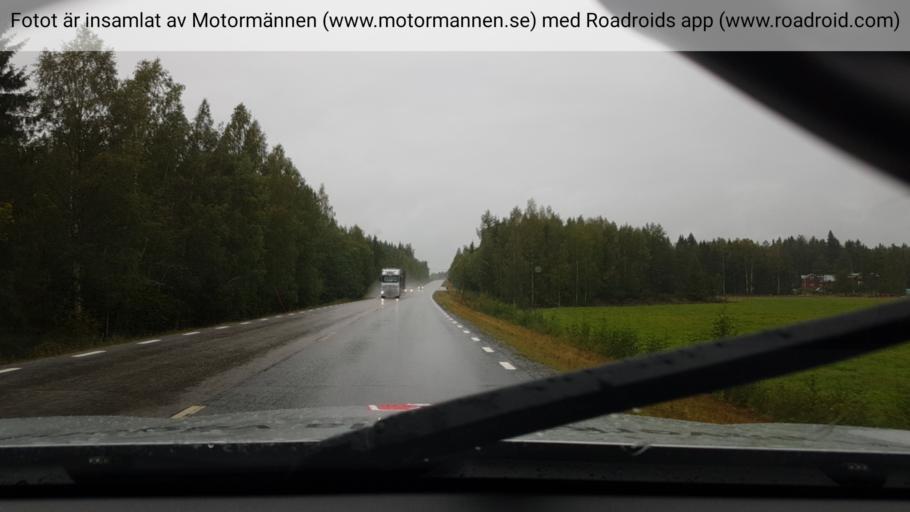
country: SE
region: Vaesterbotten
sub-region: Vannas Kommun
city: Vaennaes
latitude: 63.9217
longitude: 19.6139
